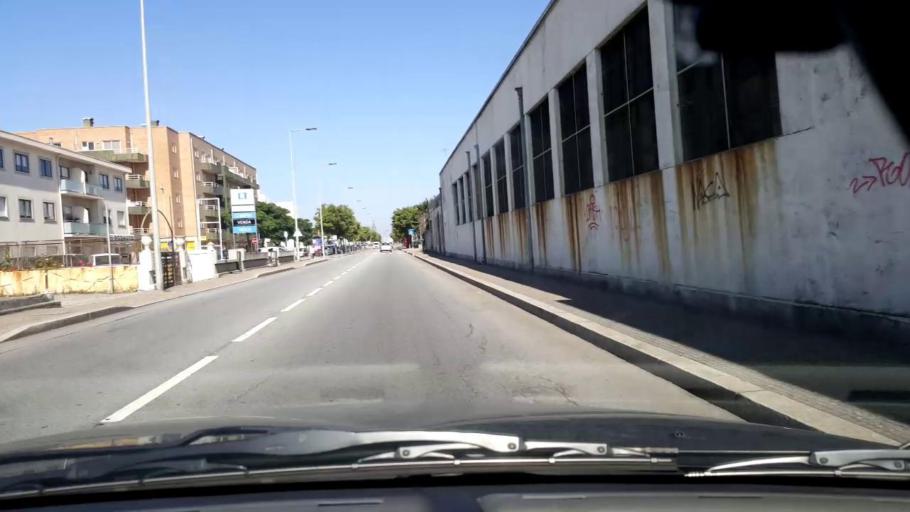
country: PT
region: Porto
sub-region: Vila do Conde
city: Vila do Conde
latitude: 41.3611
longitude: -8.7453
